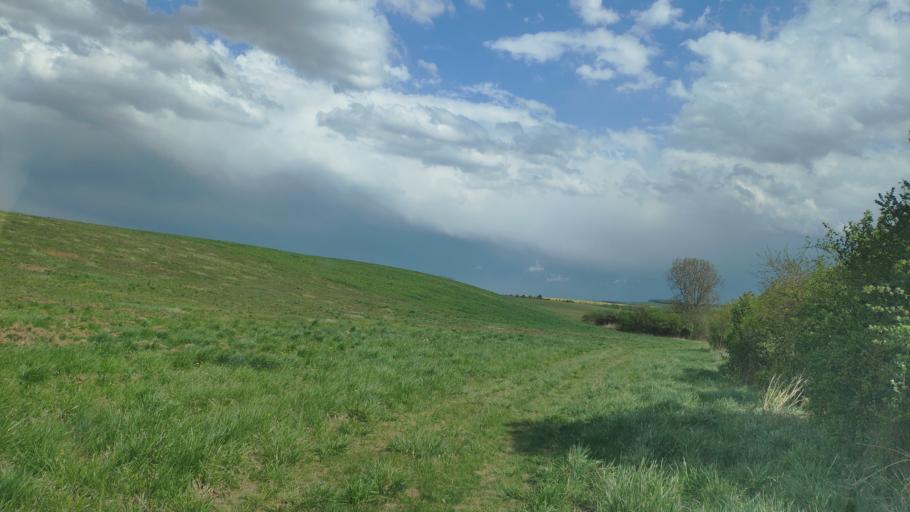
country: SK
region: Kosicky
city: Moldava nad Bodvou
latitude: 48.5563
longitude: 20.9497
